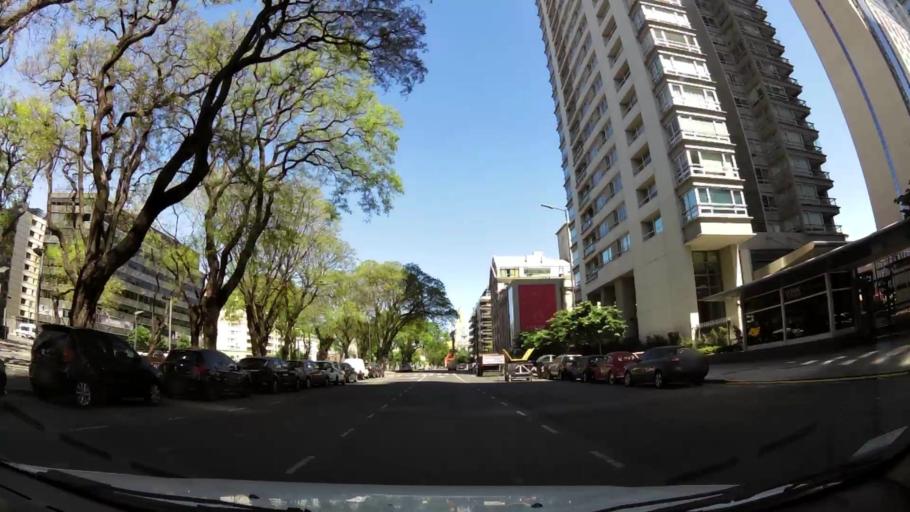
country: AR
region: Buenos Aires F.D.
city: Buenos Aires
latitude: -34.6116
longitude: -58.3611
